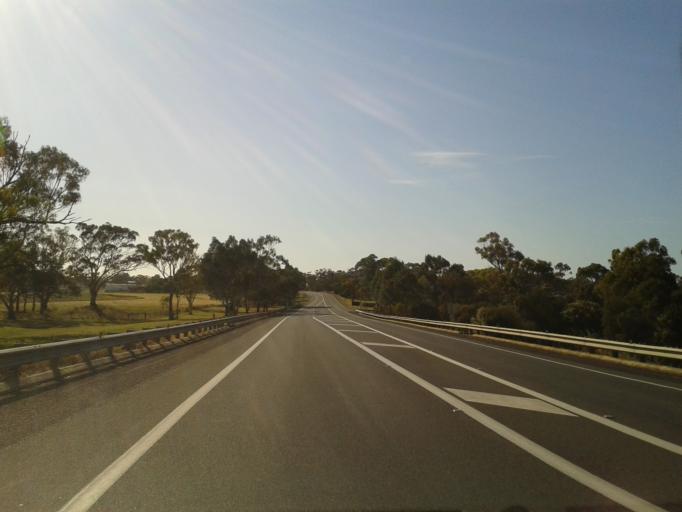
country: AU
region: South Australia
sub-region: Tatiara
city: Bordertown
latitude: -36.3074
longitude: 140.7766
